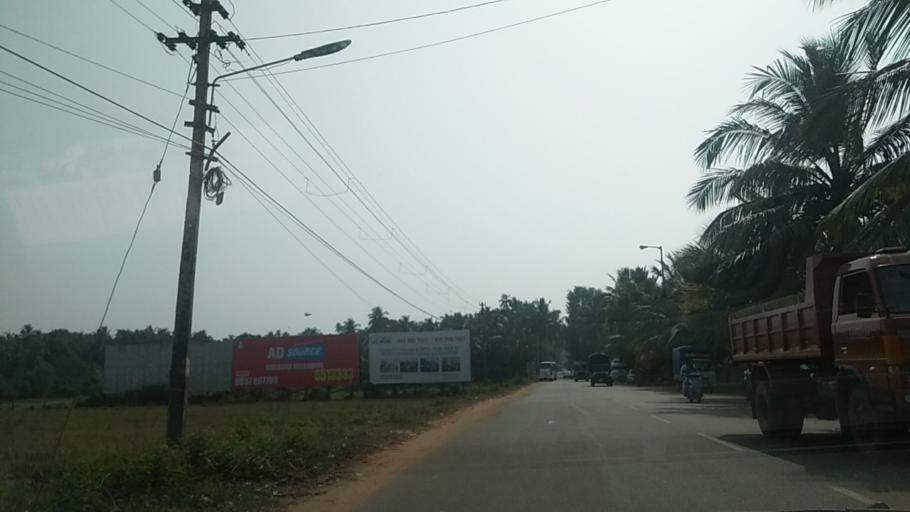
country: IN
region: Goa
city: Calangute
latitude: 15.5557
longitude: 73.7639
